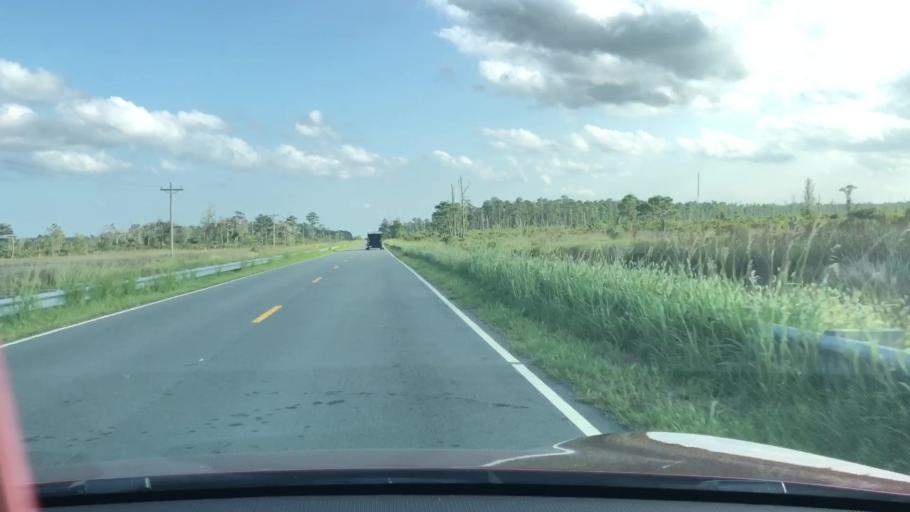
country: US
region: North Carolina
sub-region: Dare County
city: Wanchese
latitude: 35.6853
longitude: -75.7806
